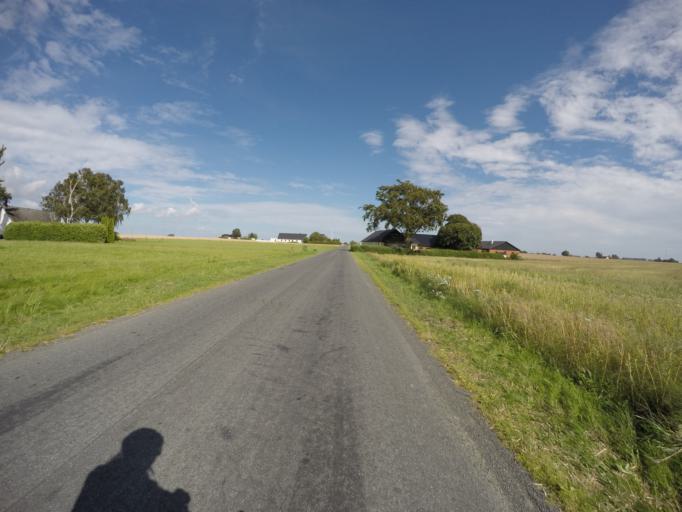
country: SE
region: Skane
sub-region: Simrishamns Kommun
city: Simrishamn
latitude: 55.4851
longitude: 14.1694
